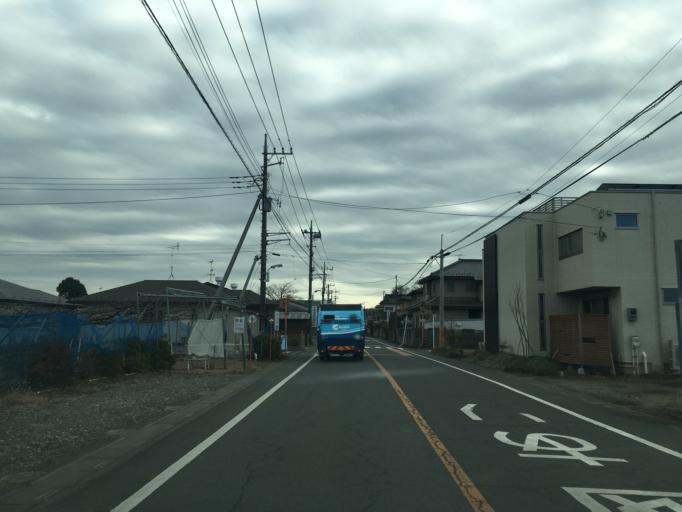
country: JP
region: Saitama
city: Sayama
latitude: 35.7959
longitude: 139.3979
